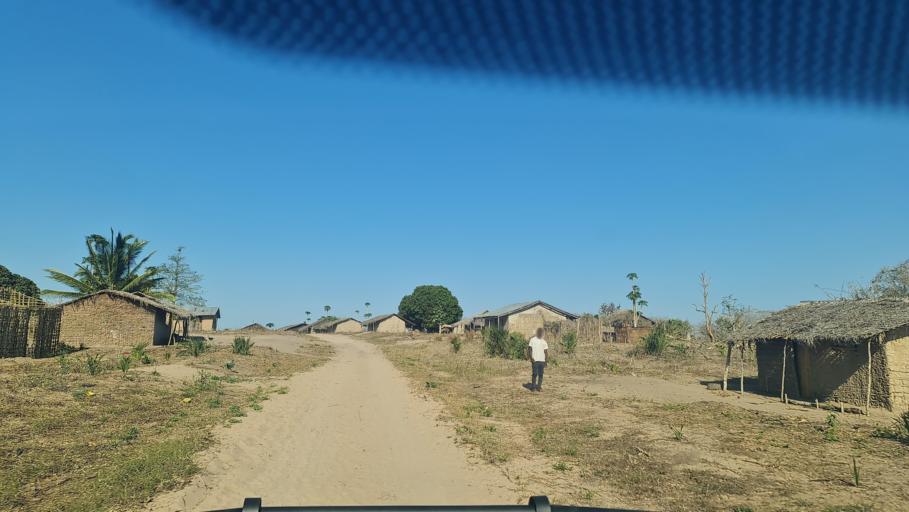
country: MZ
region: Nampula
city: Nacala
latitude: -13.9406
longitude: 40.4888
